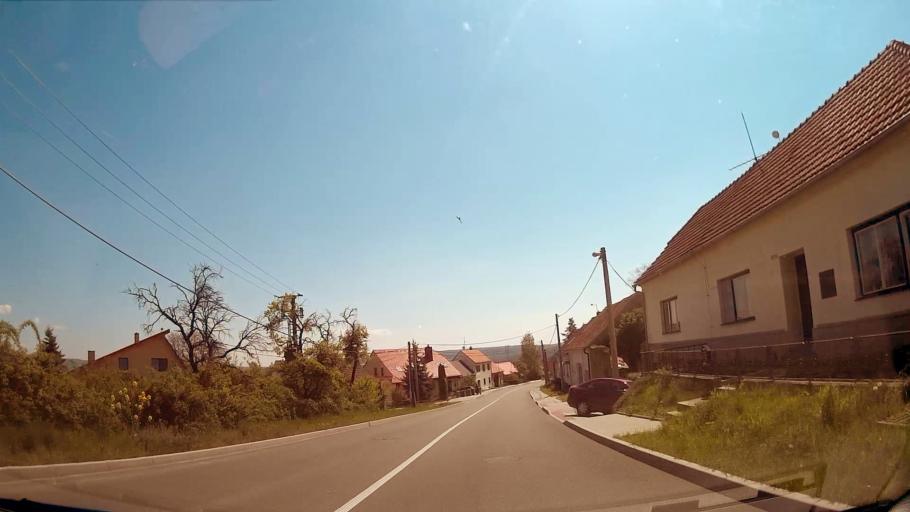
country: CZ
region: South Moravian
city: Moravsky Krumlov
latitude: 49.0722
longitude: 16.2967
